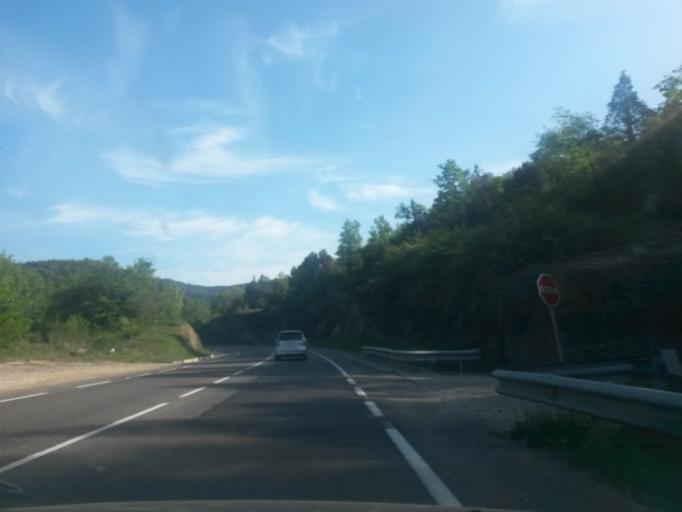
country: ES
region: Catalonia
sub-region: Provincia de Girona
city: Bas
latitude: 42.1118
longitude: 2.4901
